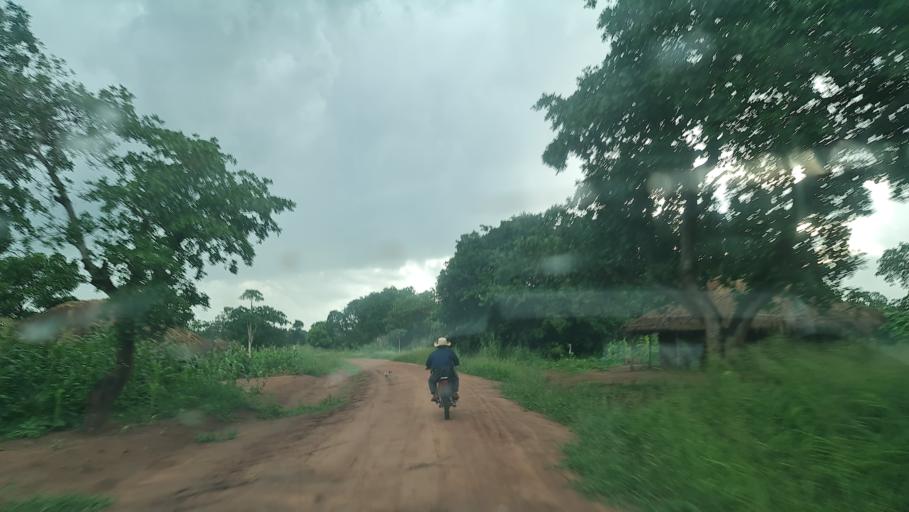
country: MZ
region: Nampula
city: Nacala
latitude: -13.9954
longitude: 40.3644
